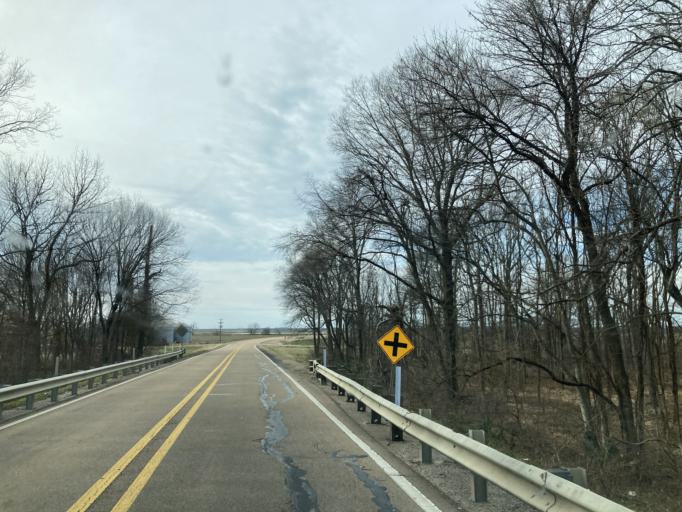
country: US
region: Mississippi
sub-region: Washington County
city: Hollandale
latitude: 33.1840
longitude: -90.6869
